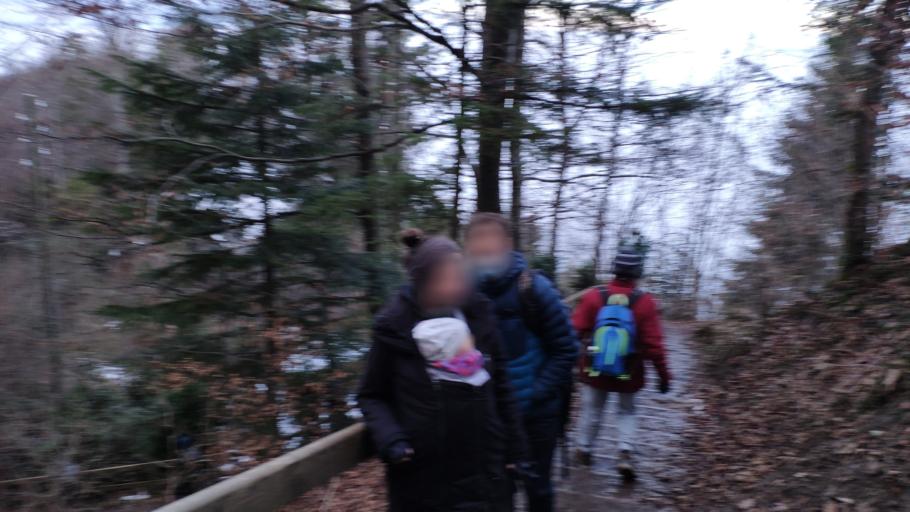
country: CH
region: Zurich
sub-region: Bezirk Affoltern
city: Sellenbueren
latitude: 47.3529
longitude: 8.4896
